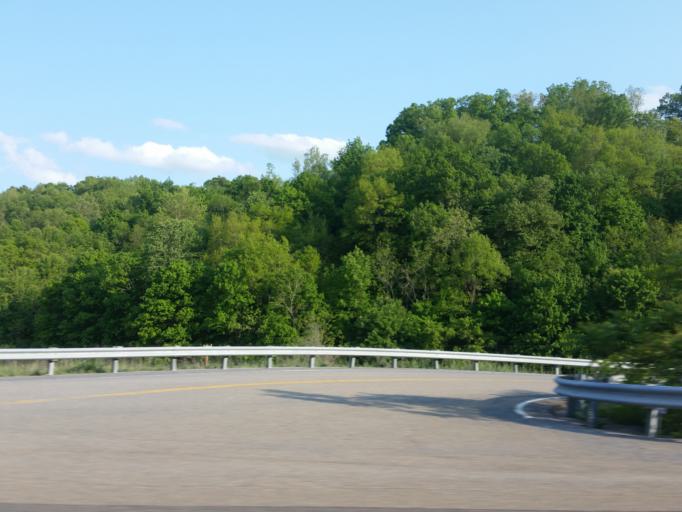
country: US
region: Virginia
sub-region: Tazewell County
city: Raven
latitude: 36.9965
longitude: -81.8317
